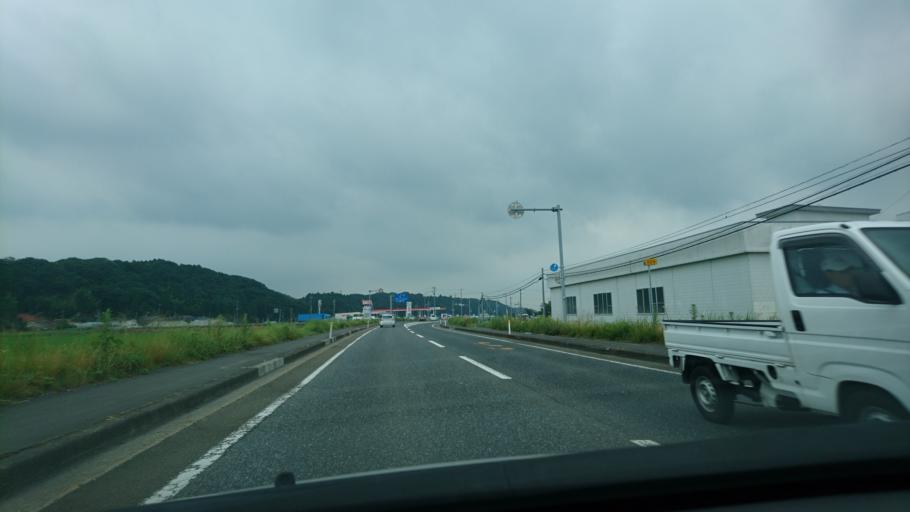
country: JP
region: Miyagi
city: Furukawa
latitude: 38.6590
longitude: 140.8784
